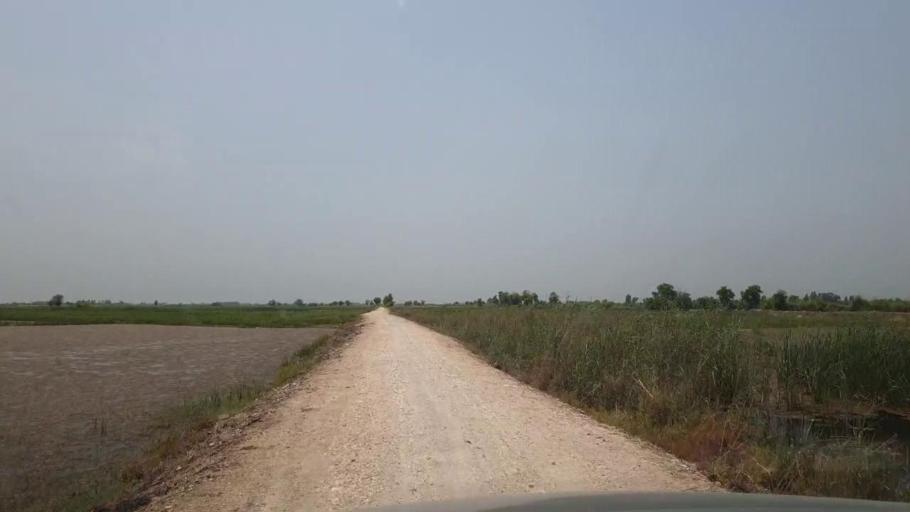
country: PK
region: Sindh
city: Garhi Yasin
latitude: 27.8687
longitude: 68.4882
